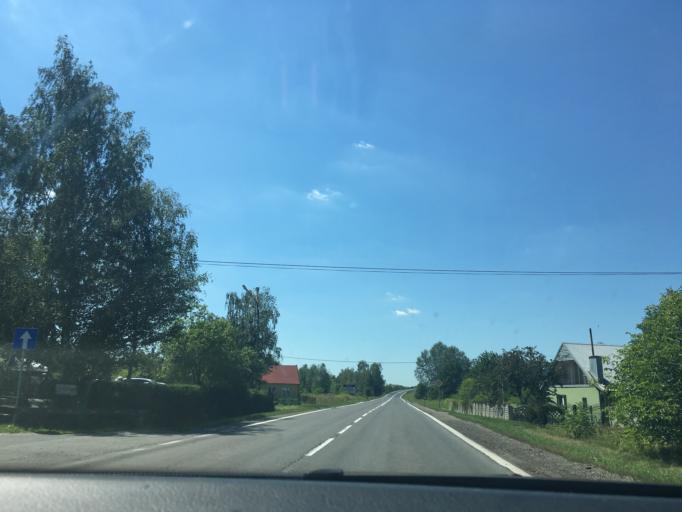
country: PL
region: Subcarpathian Voivodeship
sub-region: Powiat nizanski
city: Raclawice
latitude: 50.5146
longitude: 22.1526
